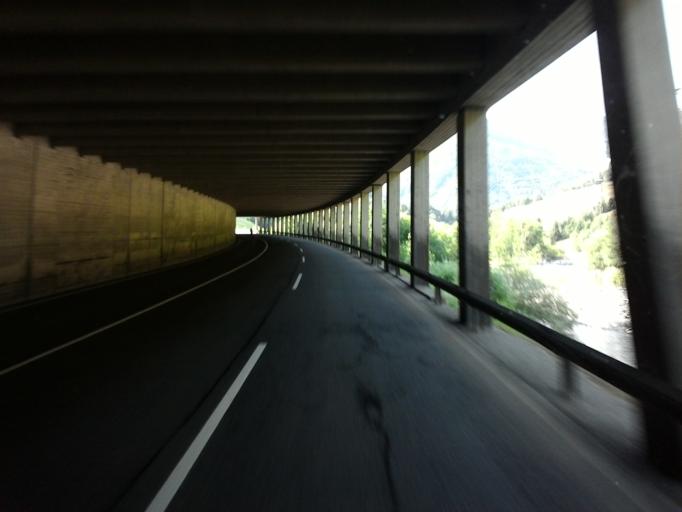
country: AT
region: Salzburg
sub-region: Politischer Bezirk Zell am See
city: Mittersill
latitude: 47.2386
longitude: 12.4912
